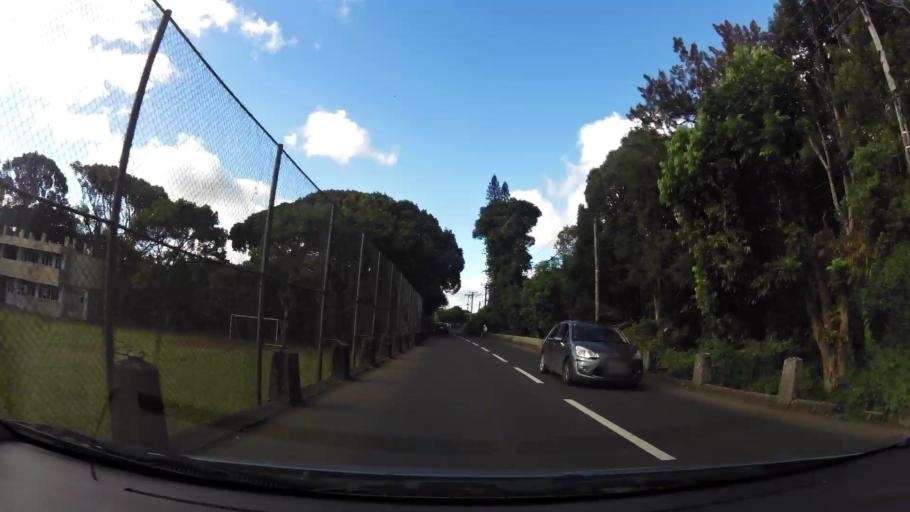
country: MU
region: Plaines Wilhems
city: Vacoas
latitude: -20.2828
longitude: 57.5003
